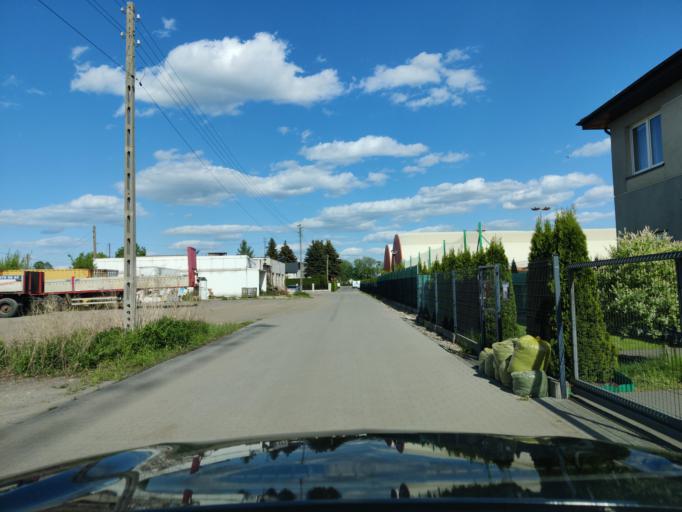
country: PL
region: Masovian Voivodeship
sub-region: Powiat legionowski
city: Stanislawow Pierwszy
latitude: 52.3374
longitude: 21.0252
